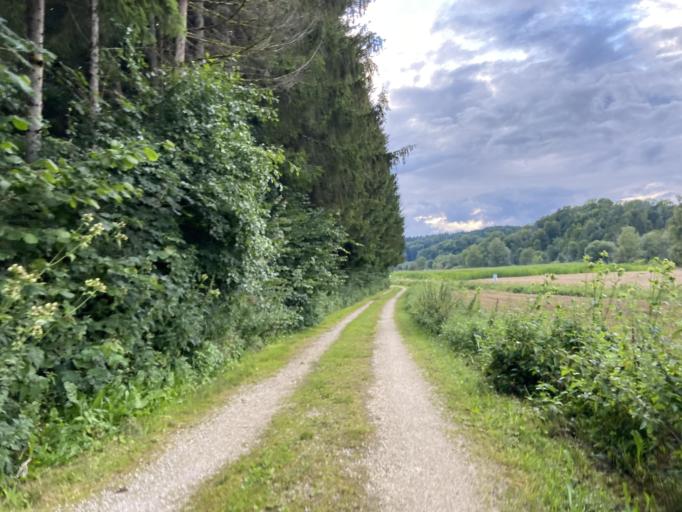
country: DE
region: Baden-Wuerttemberg
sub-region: Tuebingen Region
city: Bingen
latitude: 48.1078
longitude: 9.2661
